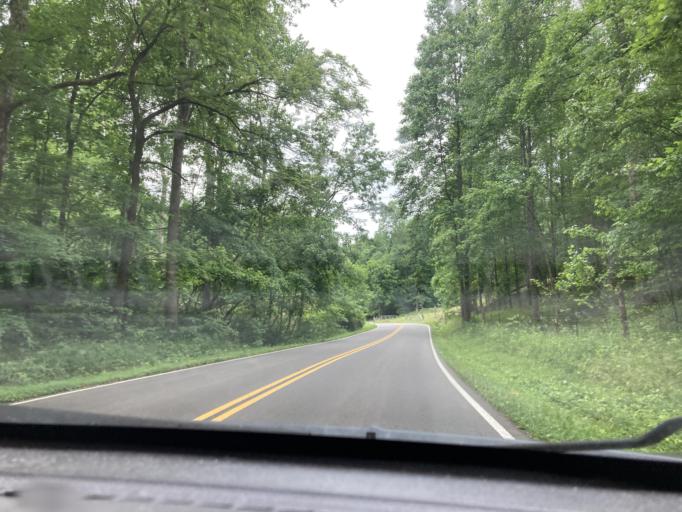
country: US
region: Tennessee
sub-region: Dickson County
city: Dickson
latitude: 36.0401
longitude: -87.3666
